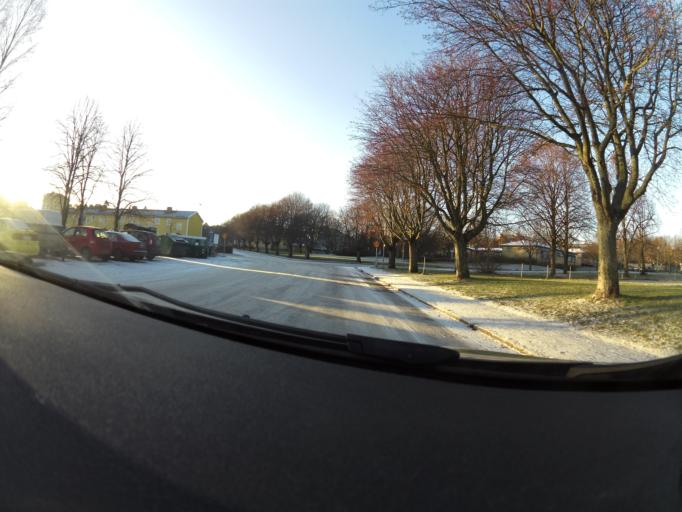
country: SE
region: Gaevleborg
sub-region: Gavle Kommun
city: Gavle
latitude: 60.6636
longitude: 17.1490
